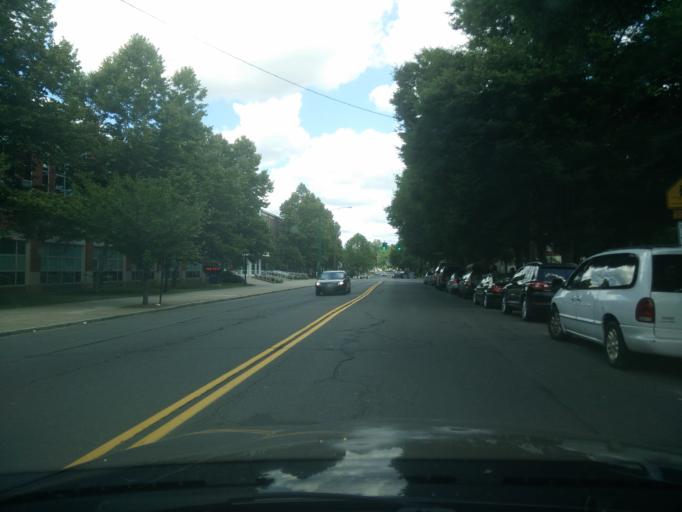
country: US
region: Connecticut
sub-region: New Haven County
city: New Haven
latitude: 41.3207
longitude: -72.9396
